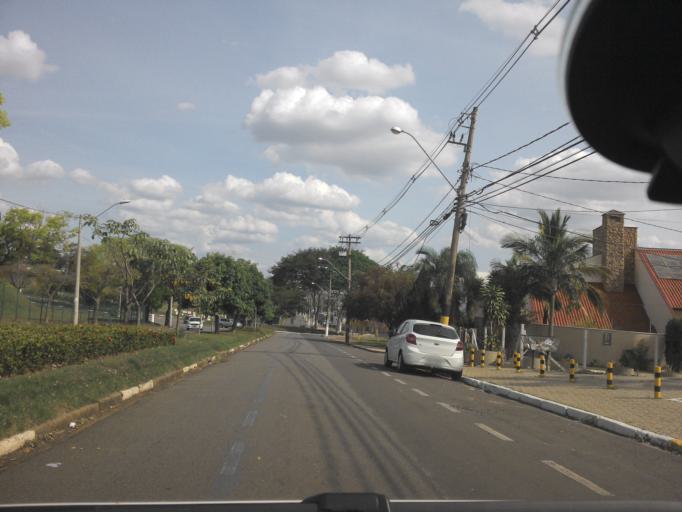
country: BR
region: Sao Paulo
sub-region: Campinas
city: Campinas
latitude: -22.8355
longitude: -47.0530
